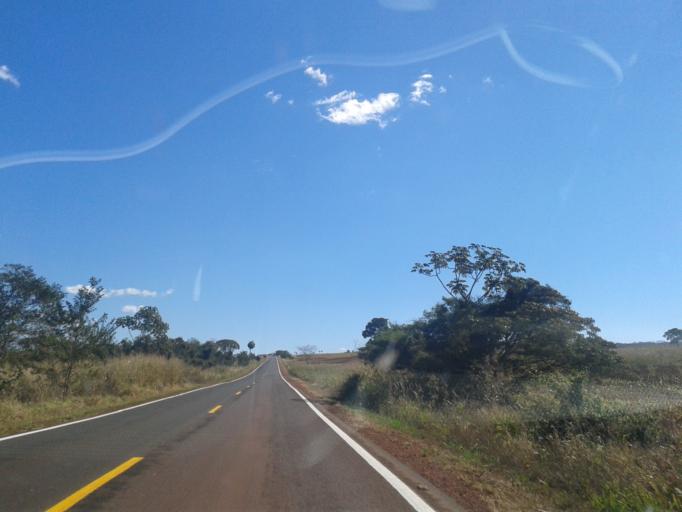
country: BR
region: Minas Gerais
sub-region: Capinopolis
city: Capinopolis
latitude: -18.6900
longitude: -49.4293
